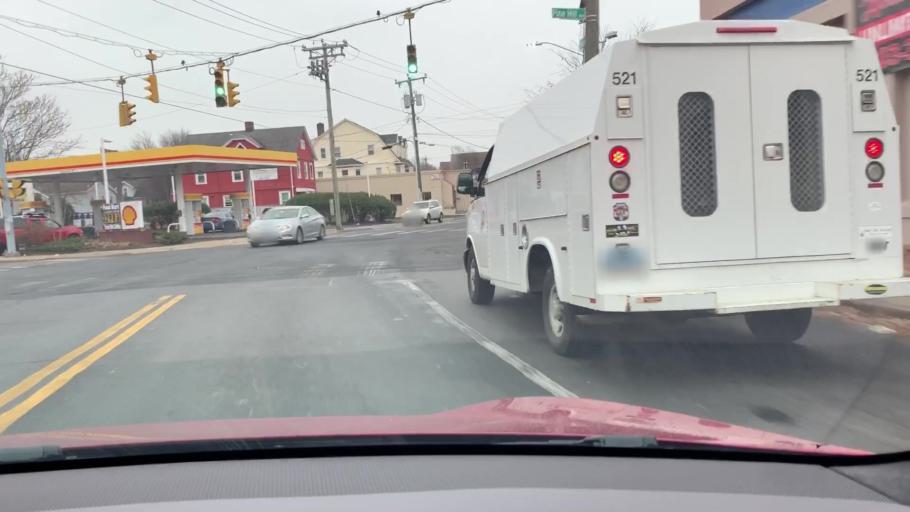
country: US
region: Connecticut
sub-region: Fairfield County
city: Stamford
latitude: 41.0717
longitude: -73.5239
